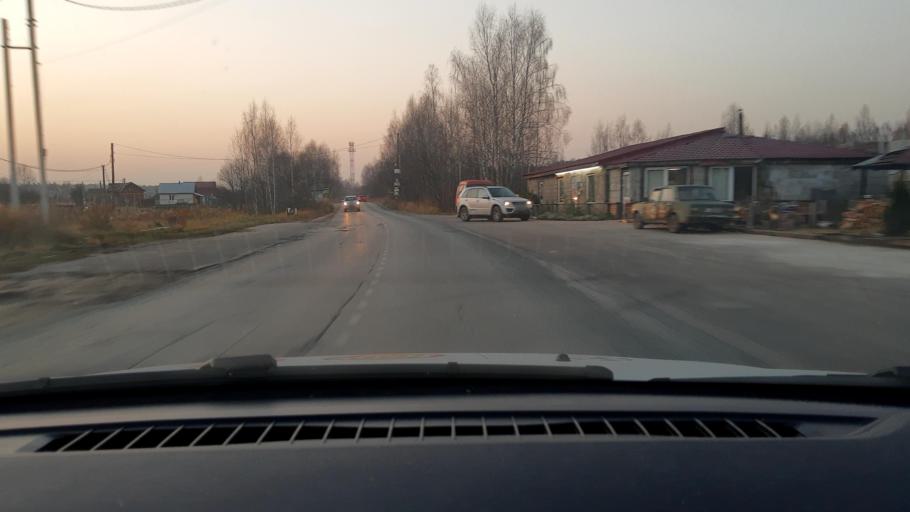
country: RU
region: Nizjnij Novgorod
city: Neklyudovo
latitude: 56.4378
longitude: 43.9188
